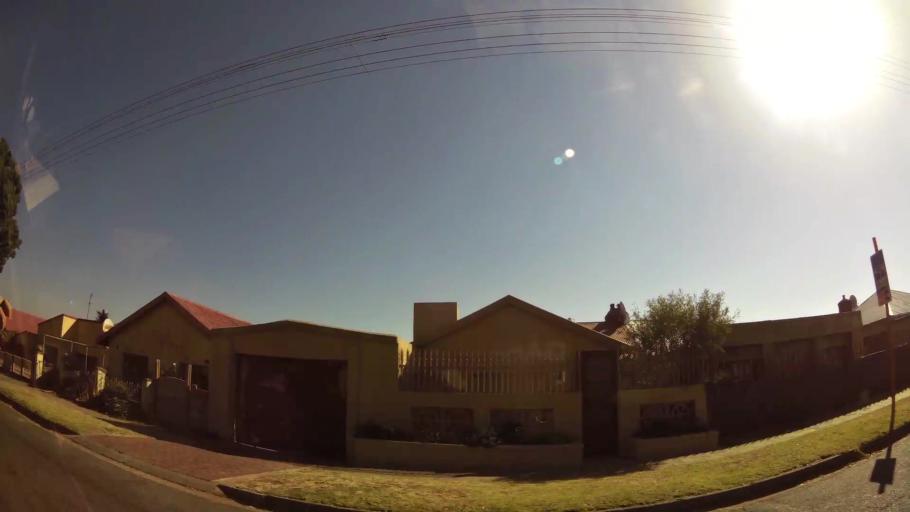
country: ZA
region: Gauteng
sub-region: City of Johannesburg Metropolitan Municipality
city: Johannesburg
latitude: -26.1887
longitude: 27.9780
